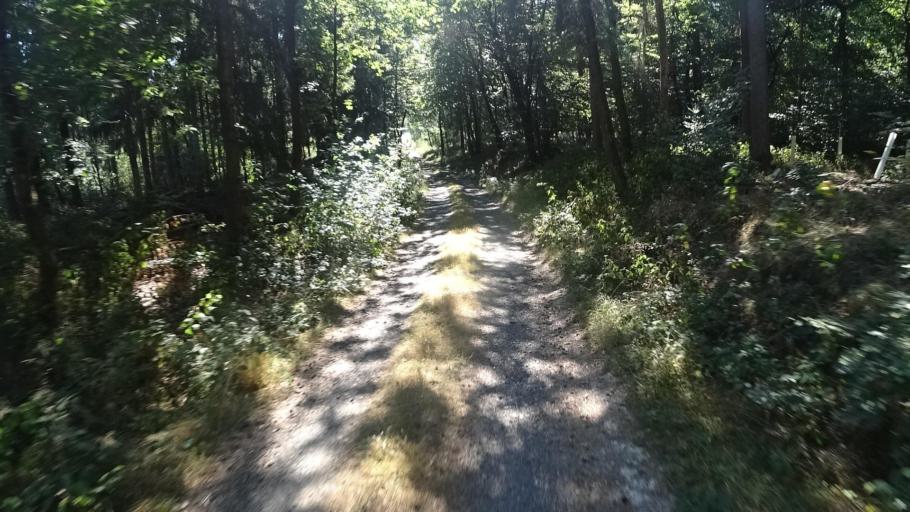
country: DE
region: Rheinland-Pfalz
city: Reich
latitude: 49.9891
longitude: 7.4308
